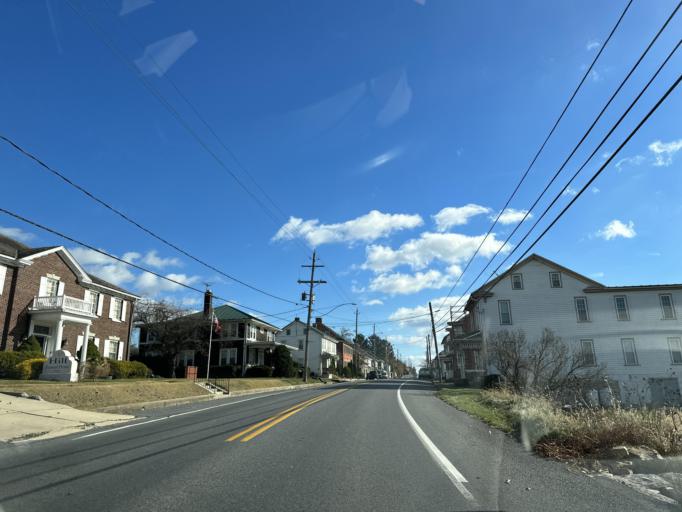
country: US
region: Pennsylvania
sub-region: Lebanon County
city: Myerstown
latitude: 40.4590
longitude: -76.2497
